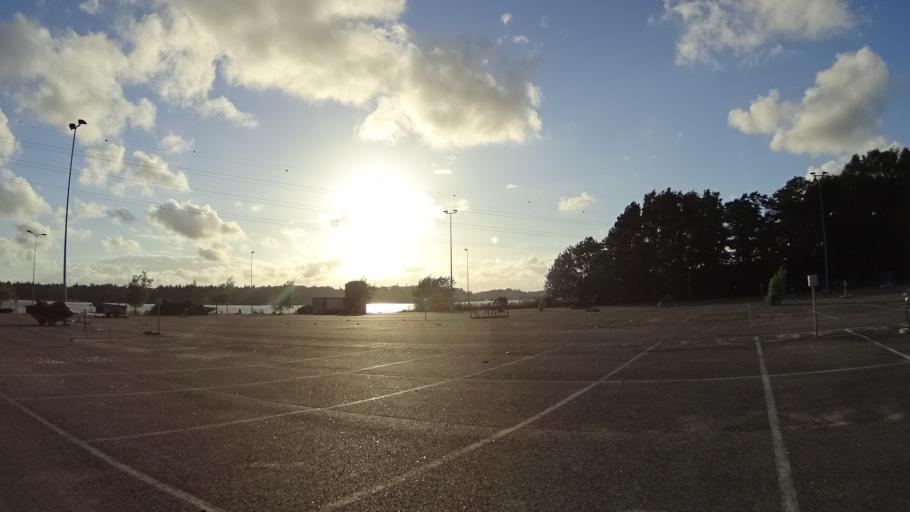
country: FI
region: Uusimaa
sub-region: Helsinki
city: Helsinki
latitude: 60.1811
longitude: 24.9038
